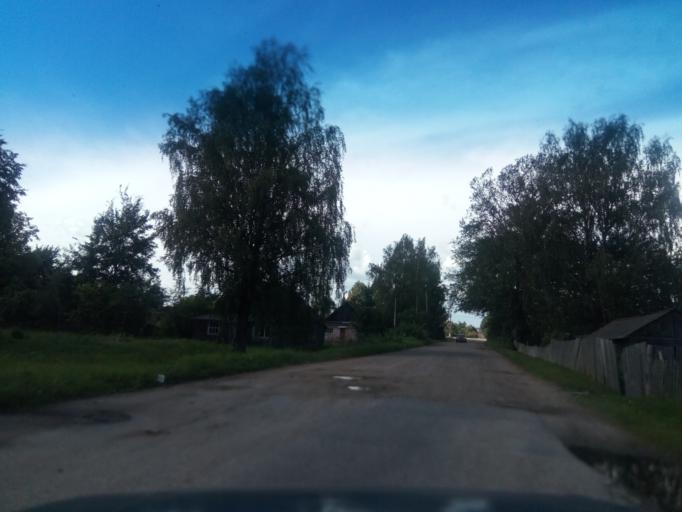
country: BY
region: Vitebsk
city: Dzisna
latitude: 55.6741
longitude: 28.3333
